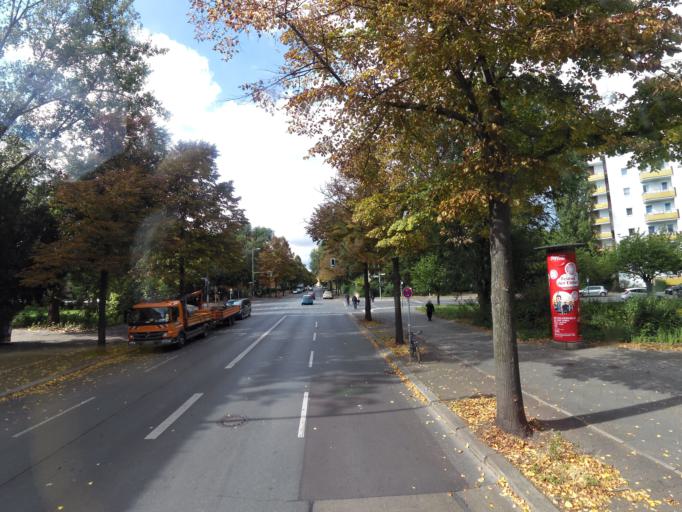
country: DE
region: Berlin
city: Bezirk Kreuzberg
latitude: 52.5050
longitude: 13.4060
